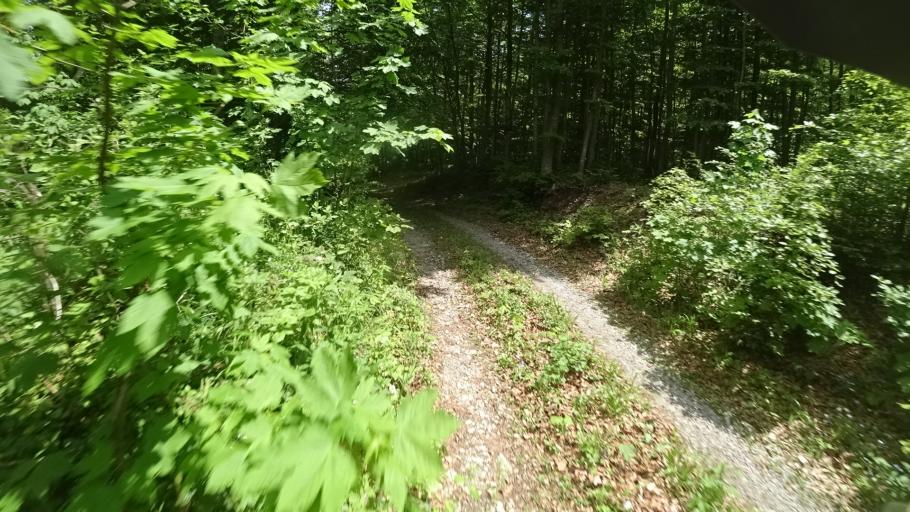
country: HR
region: Zadarska
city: Gracac
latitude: 44.4688
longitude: 15.8941
